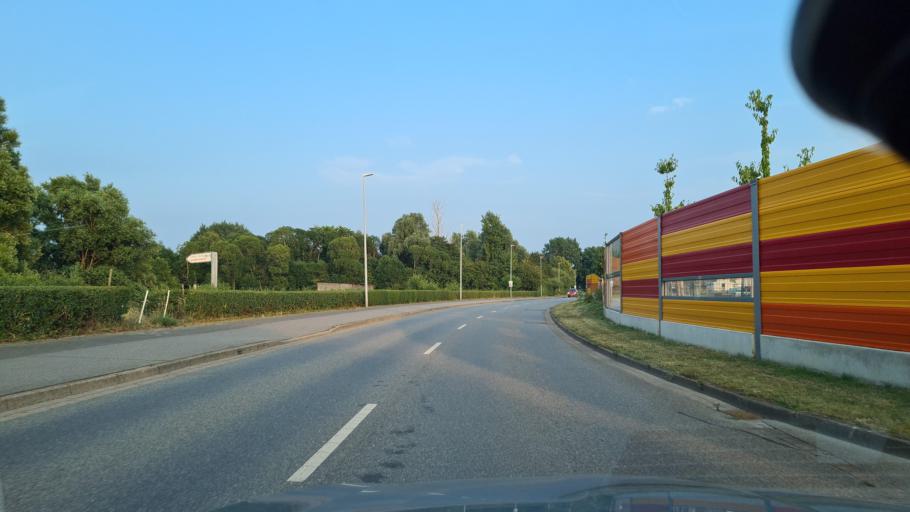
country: DE
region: Schleswig-Holstein
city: Husum
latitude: 54.4941
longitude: 9.0315
